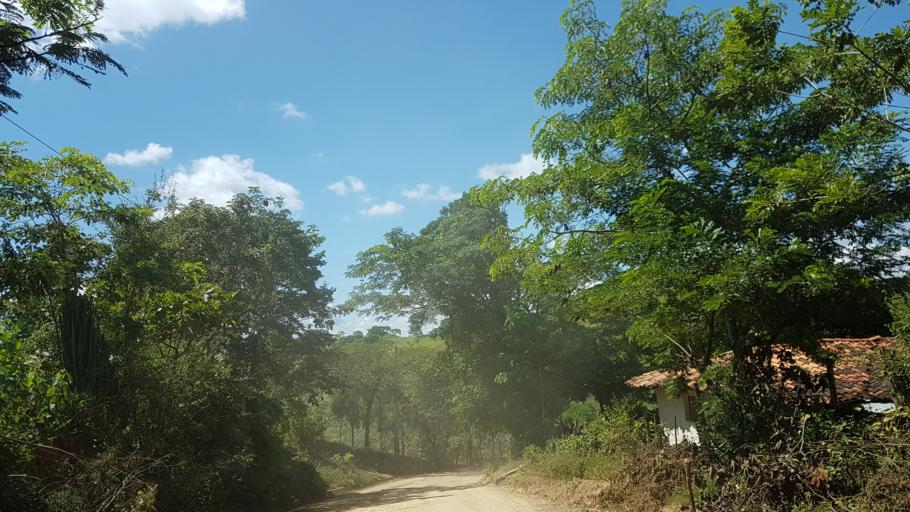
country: HN
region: El Paraiso
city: Santa Cruz
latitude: 13.7315
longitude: -86.6905
